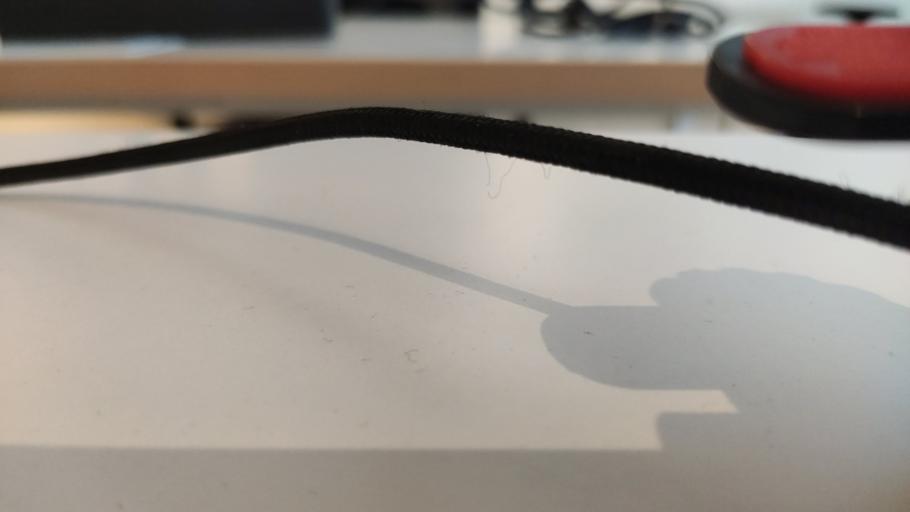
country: RU
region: Moskovskaya
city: Novopetrovskoye
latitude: 55.9478
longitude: 36.4371
